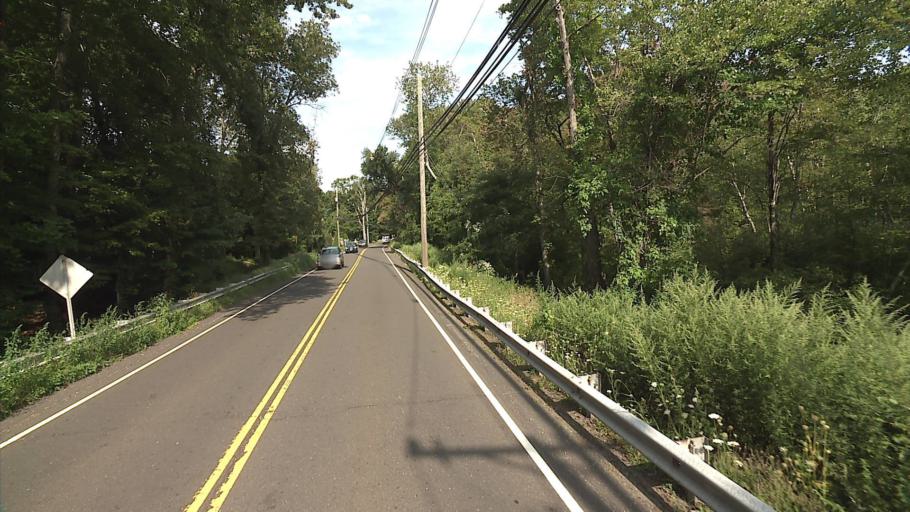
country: US
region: Connecticut
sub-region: Fairfield County
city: New Canaan
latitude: 41.1841
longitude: -73.5022
